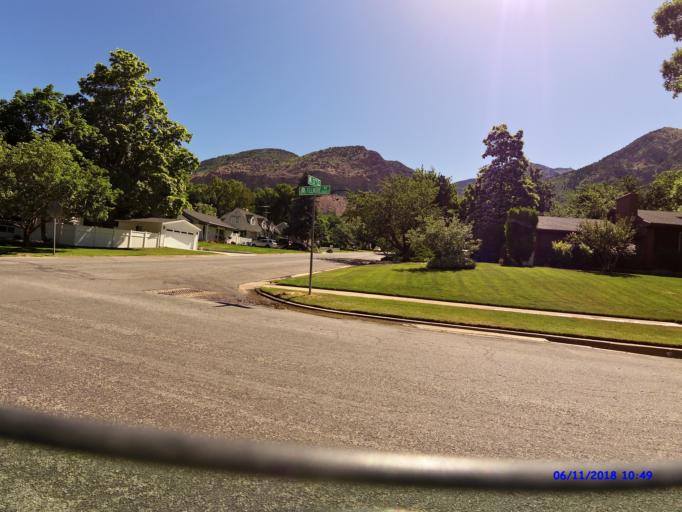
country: US
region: Utah
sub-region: Weber County
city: Ogden
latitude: 41.2159
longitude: -111.9374
